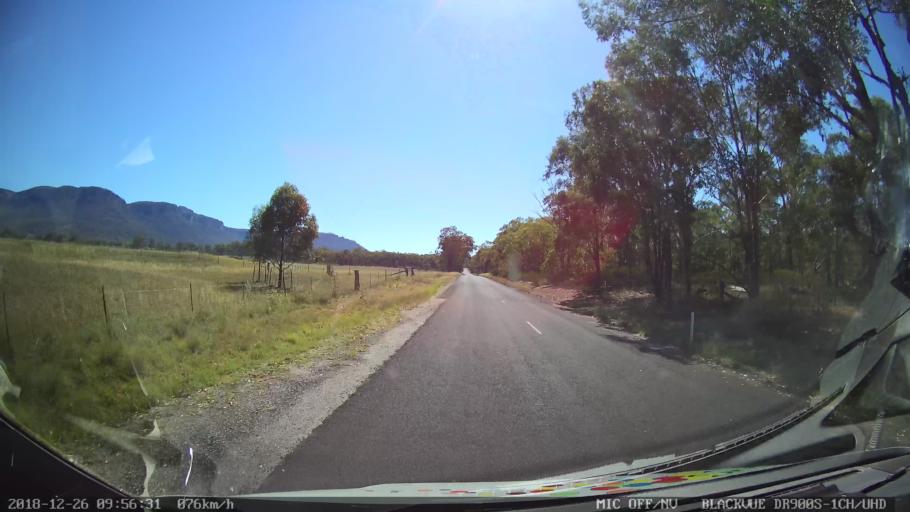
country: AU
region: New South Wales
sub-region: Mid-Western Regional
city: Kandos
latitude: -33.0404
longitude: 150.1802
